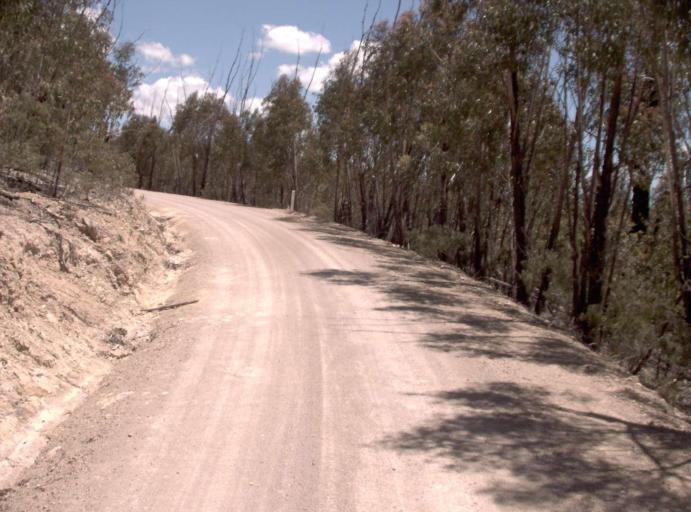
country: AU
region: New South Wales
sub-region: Snowy River
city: Jindabyne
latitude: -37.0832
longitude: 148.3289
